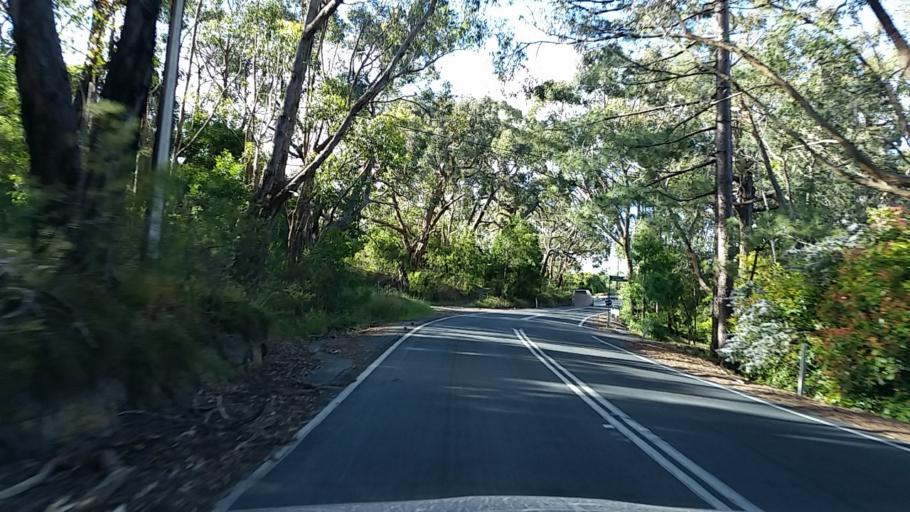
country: AU
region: South Australia
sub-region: Adelaide Hills
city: Stirling
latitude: -35.0225
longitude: 138.7544
